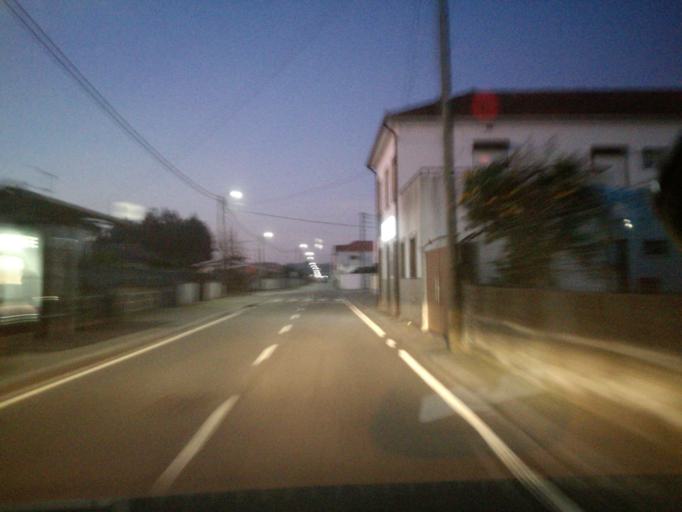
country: PT
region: Porto
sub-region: Maia
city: Nogueira
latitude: 41.2419
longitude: -8.5866
